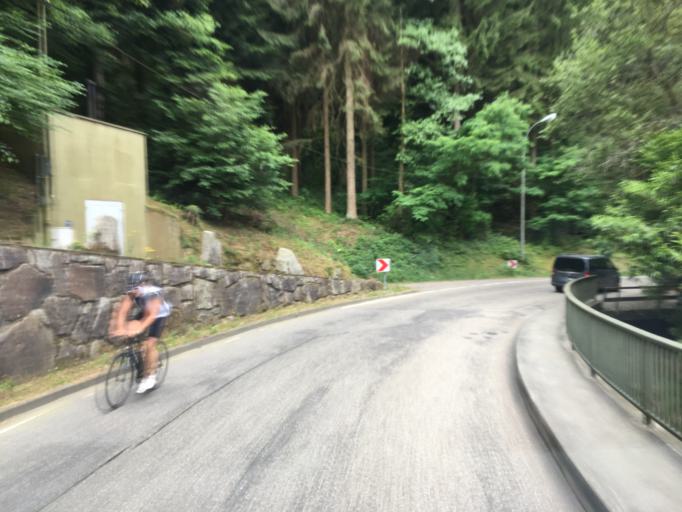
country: DE
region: Baden-Wuerttemberg
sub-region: Karlsruhe Region
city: Buhlertal
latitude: 48.7149
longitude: 8.2010
